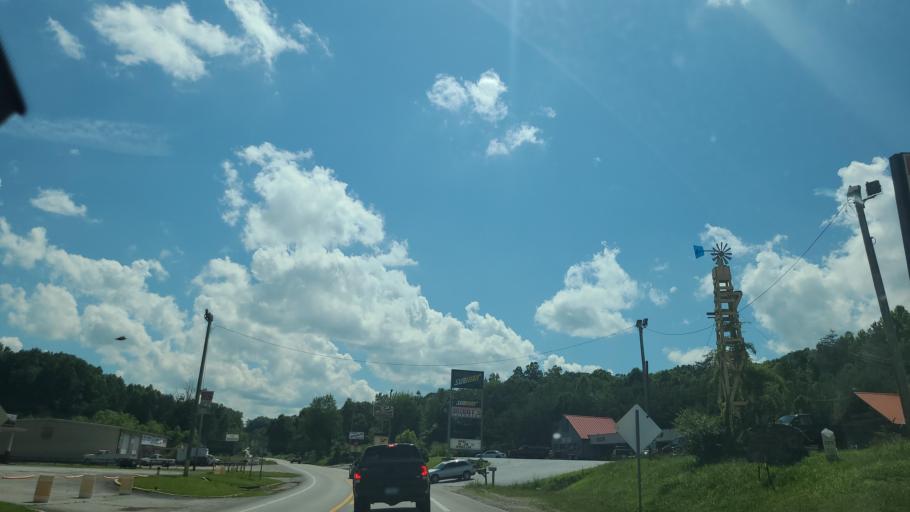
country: US
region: Kentucky
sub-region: Whitley County
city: Corbin
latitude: 36.9177
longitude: -84.1331
